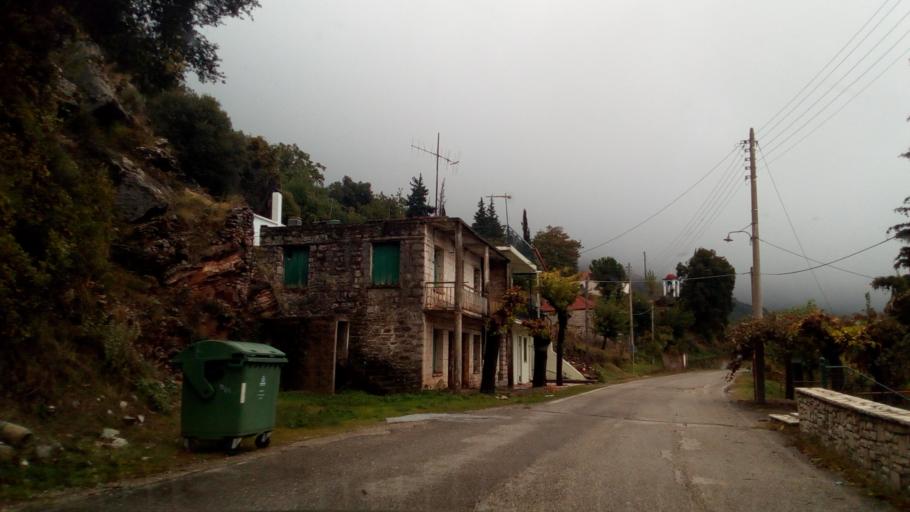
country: GR
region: West Greece
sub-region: Nomos Aitolias kai Akarnanias
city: Nafpaktos
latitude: 38.5190
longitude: 21.8444
